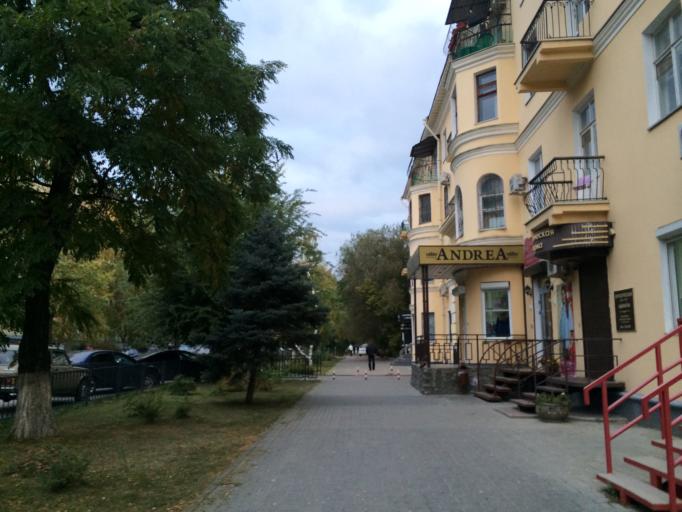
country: RU
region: Volgograd
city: Volgograd
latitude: 48.7126
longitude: 44.5216
